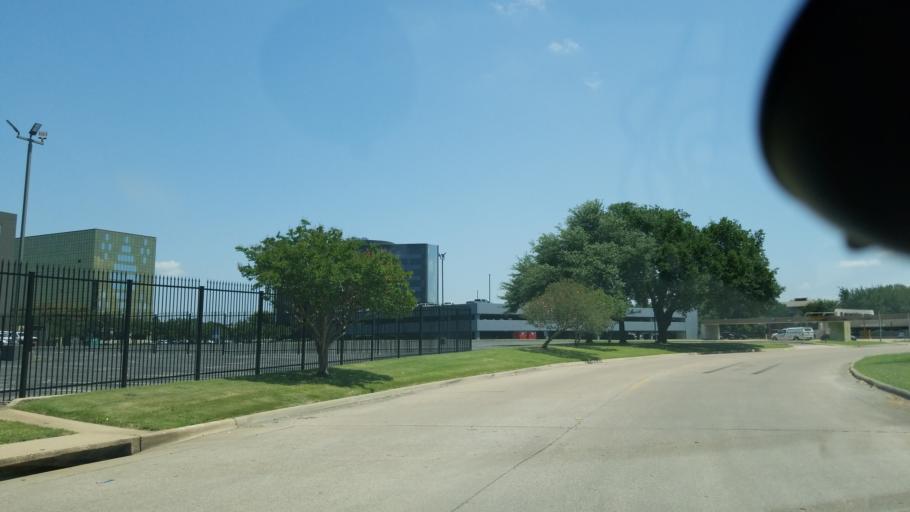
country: US
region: Texas
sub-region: Dallas County
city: Dallas
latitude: 32.8193
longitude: -96.8655
